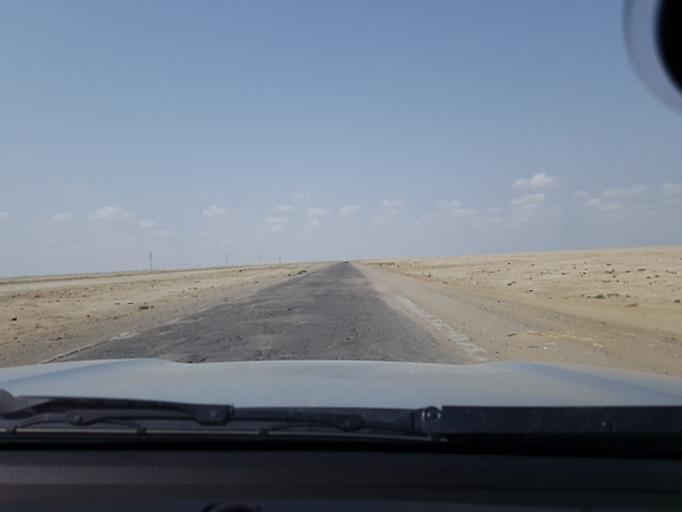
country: TM
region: Balkan
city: Gumdag
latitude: 38.6417
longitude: 54.3761
